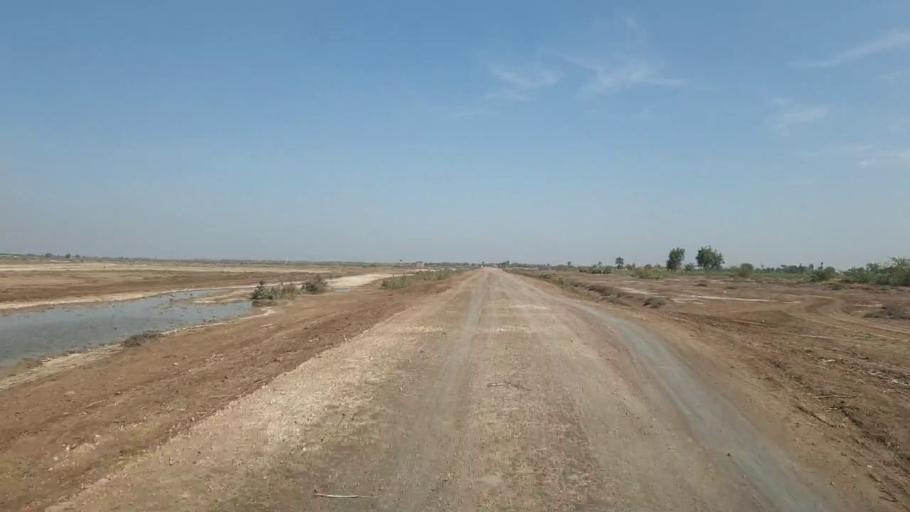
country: PK
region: Sindh
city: Samaro
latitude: 25.3602
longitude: 69.2546
